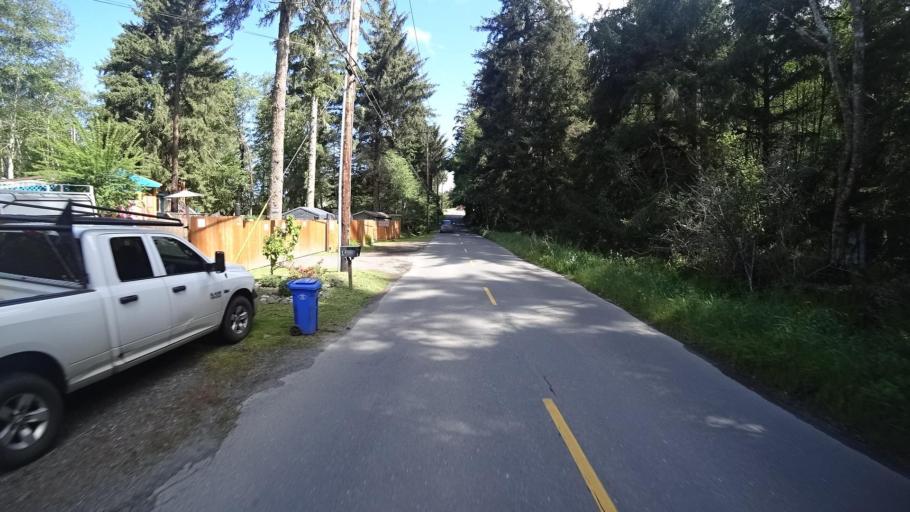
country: US
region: California
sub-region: Humboldt County
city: McKinleyville
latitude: 40.9313
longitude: -124.0816
